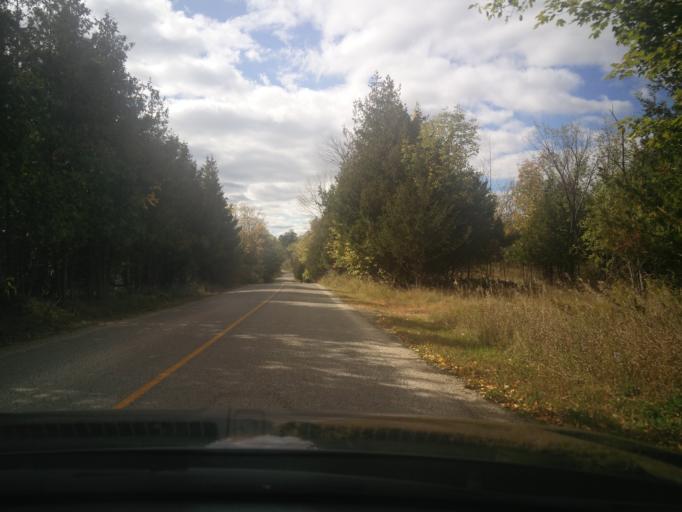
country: CA
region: Ontario
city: Perth
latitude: 44.6577
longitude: -76.5536
